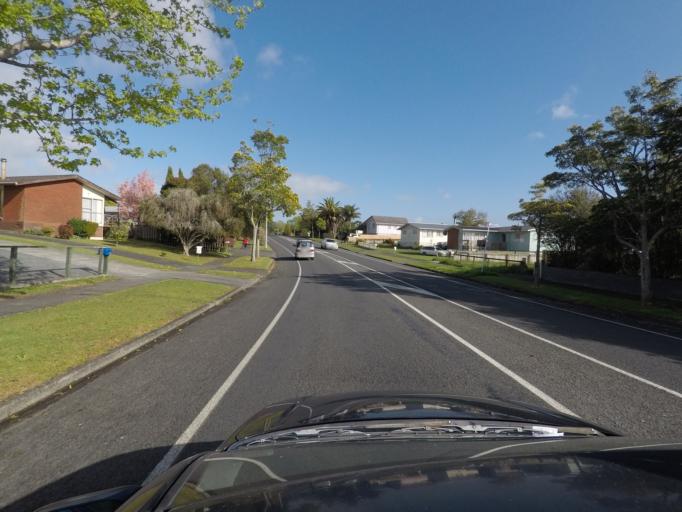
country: NZ
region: Northland
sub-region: Whangarei
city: Whangarei
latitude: -35.6846
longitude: 174.3253
